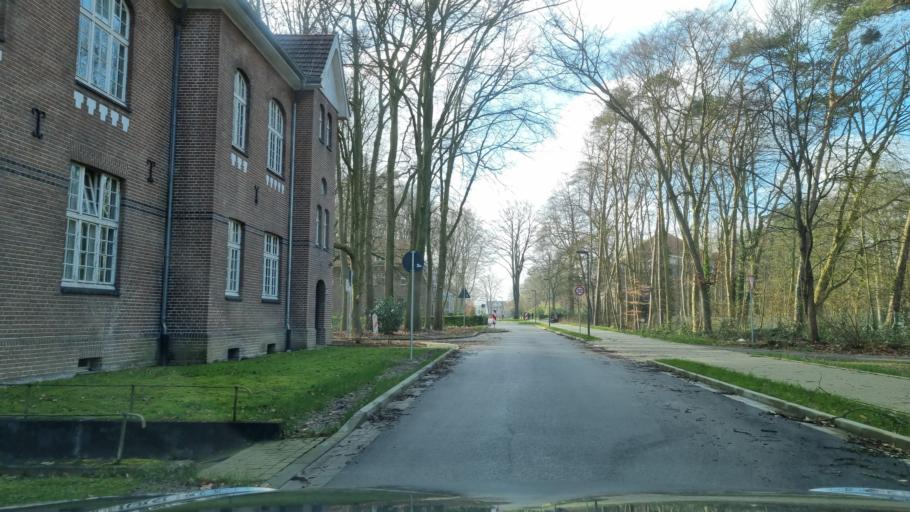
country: DE
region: North Rhine-Westphalia
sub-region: Regierungsbezirk Dusseldorf
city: Kleve
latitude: 51.7598
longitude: 6.1806
